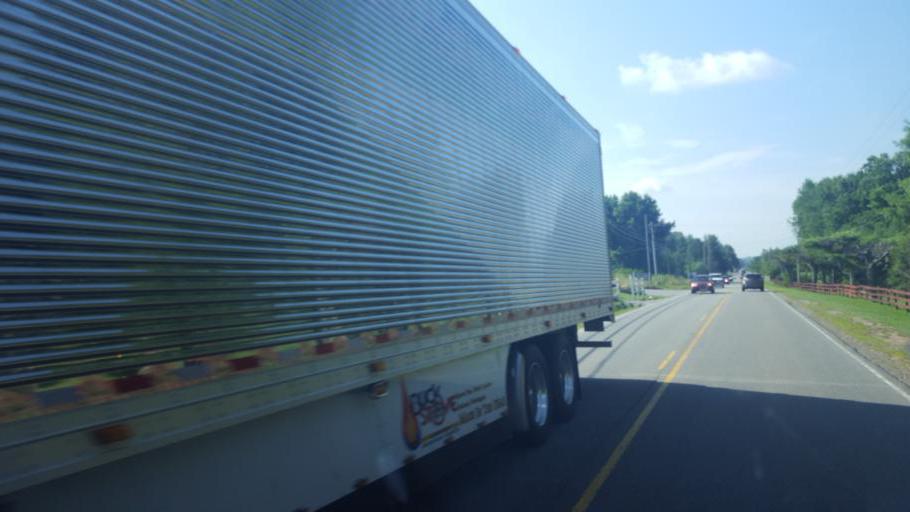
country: US
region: North Carolina
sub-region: Avery County
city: Newland
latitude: 36.1221
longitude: -81.9339
